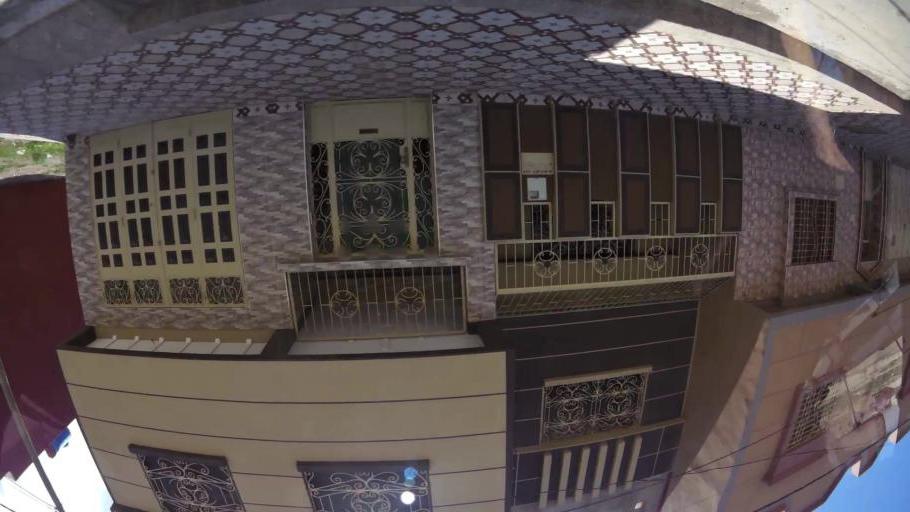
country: MA
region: Oriental
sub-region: Oujda-Angad
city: Oujda
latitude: 34.6954
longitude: -1.8939
